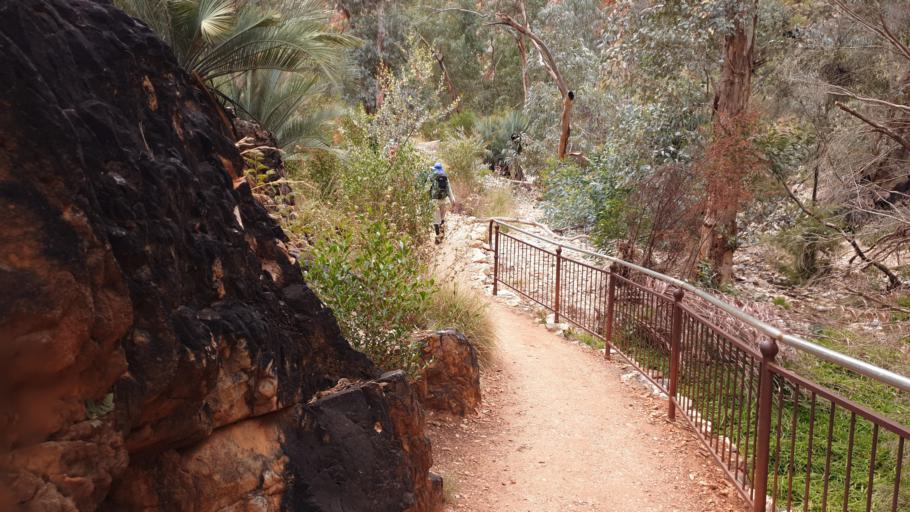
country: AU
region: Northern Territory
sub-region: Alice Springs
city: Alice Springs
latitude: -23.7174
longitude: 133.4704
